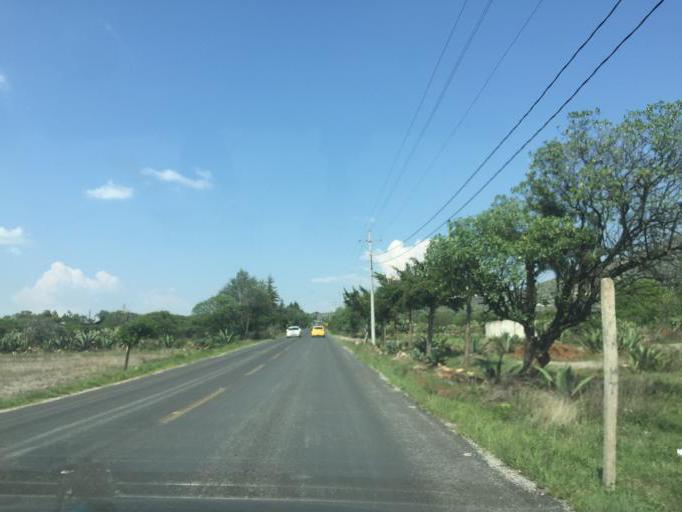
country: MX
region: Hidalgo
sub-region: Cardonal
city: Pozuelos
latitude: 20.6126
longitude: -99.0813
